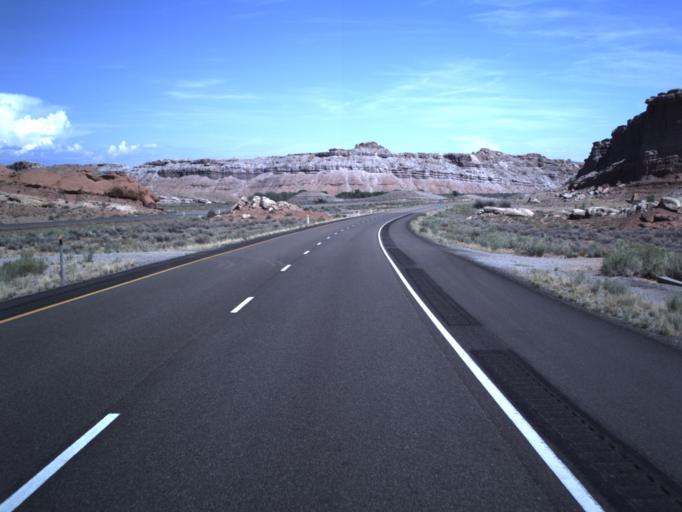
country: US
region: Utah
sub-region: Carbon County
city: East Carbon City
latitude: 38.9243
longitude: -110.4191
